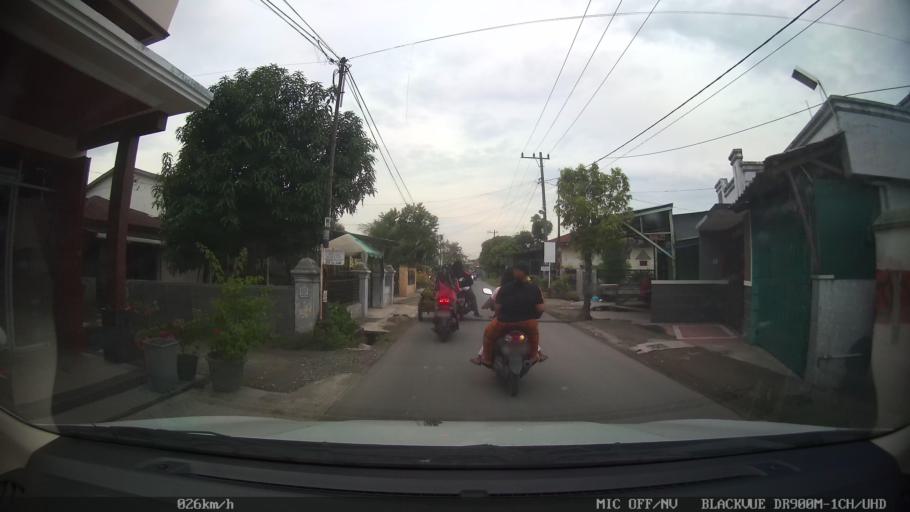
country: ID
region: North Sumatra
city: Sunggal
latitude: 3.6119
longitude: 98.6010
